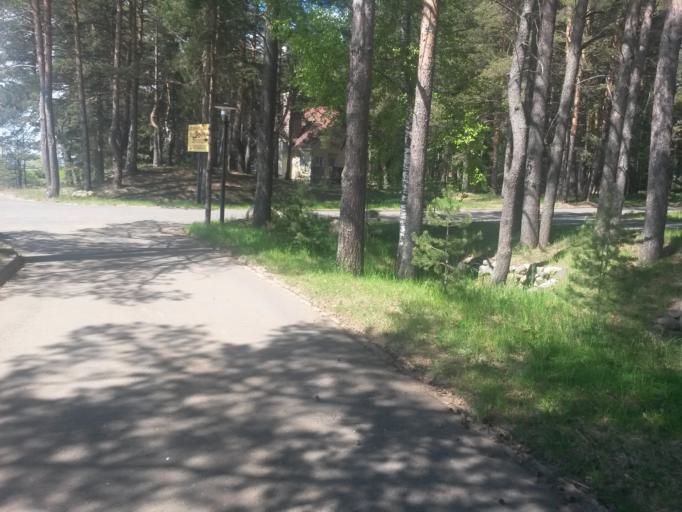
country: RU
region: Jaroslavl
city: Borok
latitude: 58.0622
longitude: 38.3471
